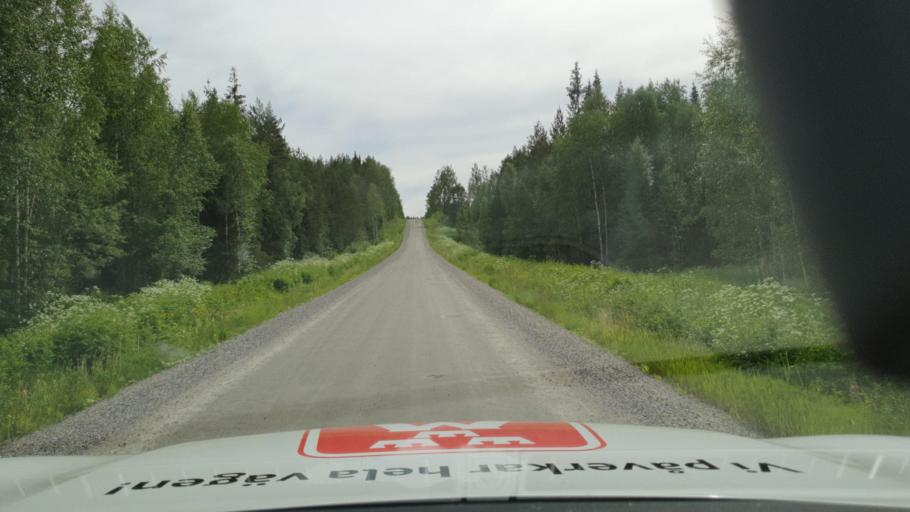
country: SE
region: Vaesterbotten
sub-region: Skelleftea Kommun
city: Burea
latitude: 64.4467
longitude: 21.0224
